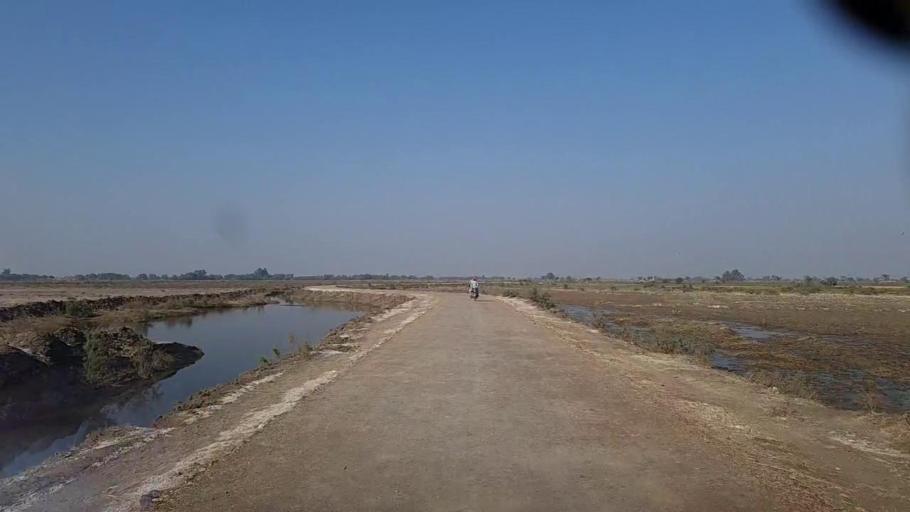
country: PK
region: Sindh
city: Jacobabad
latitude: 28.3060
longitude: 68.5615
